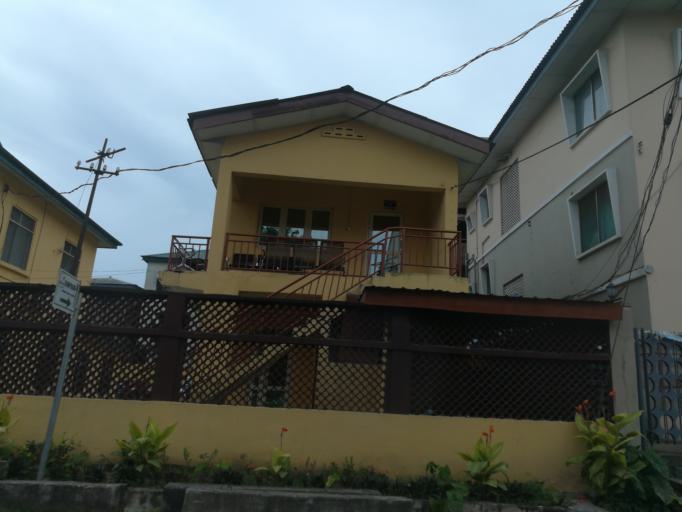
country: NG
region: Lagos
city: Ebute Metta
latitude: 6.4882
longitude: 3.3822
